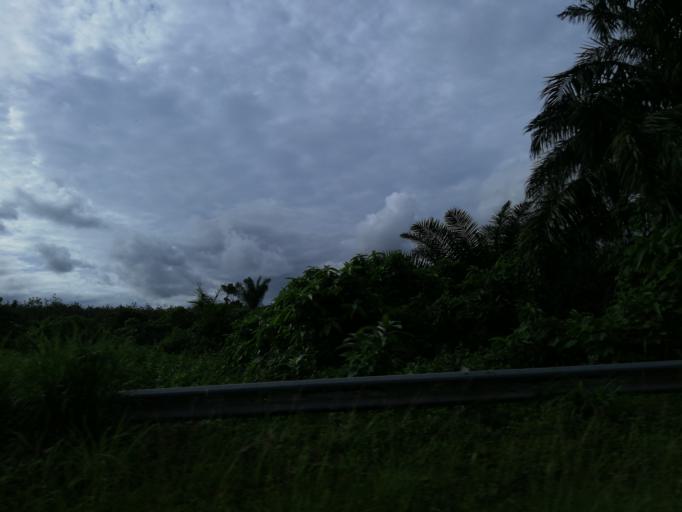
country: MY
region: Penang
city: Tasek Glugor
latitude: 5.5016
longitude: 100.6146
